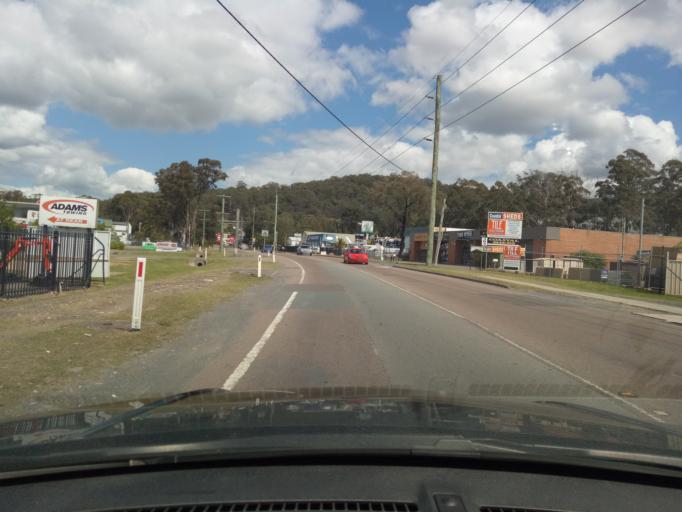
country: AU
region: New South Wales
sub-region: Gosford Shire
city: Gosford
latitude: -33.4172
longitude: 151.3231
